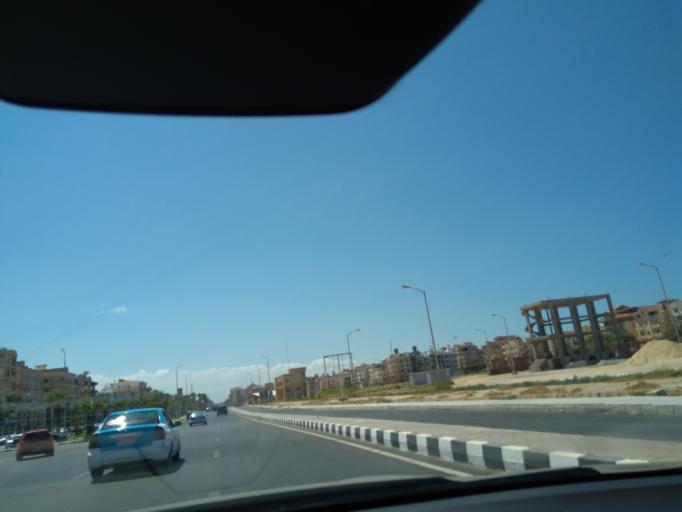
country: EG
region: Dumyat
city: Faraskur
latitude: 31.4403
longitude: 31.6768
